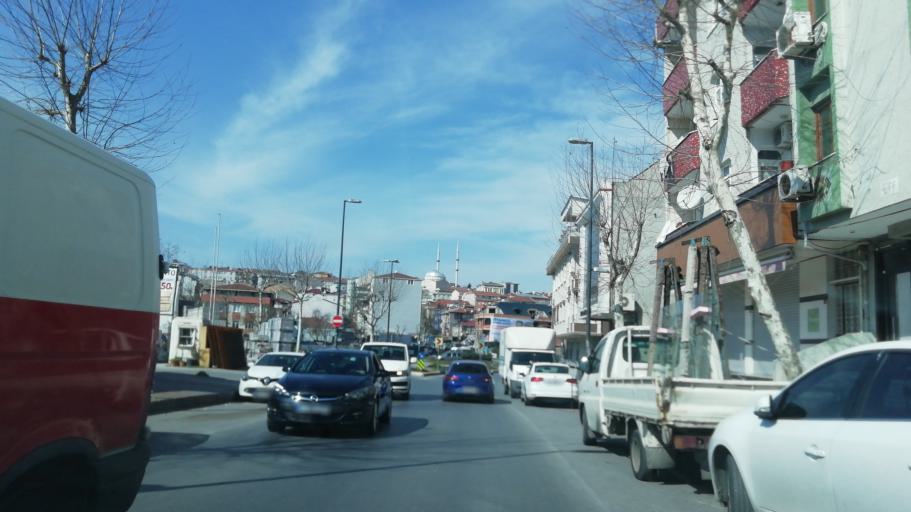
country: TR
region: Istanbul
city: Bahcelievler
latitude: 41.0164
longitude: 28.8497
